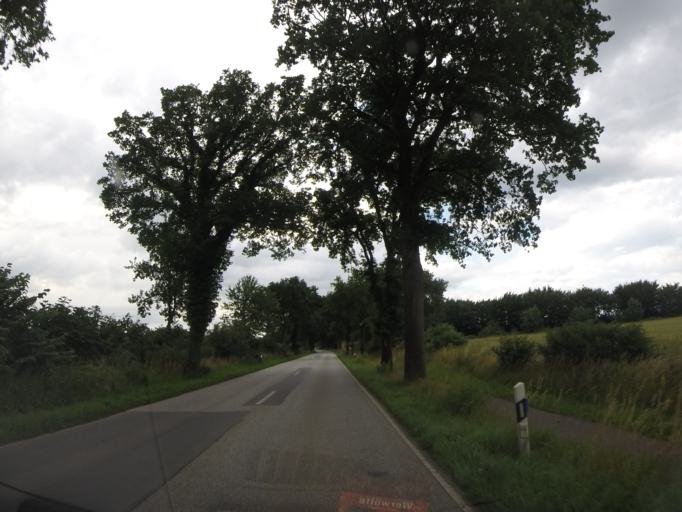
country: DE
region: Schleswig-Holstein
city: Ratekau
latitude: 53.9678
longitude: 10.7183
